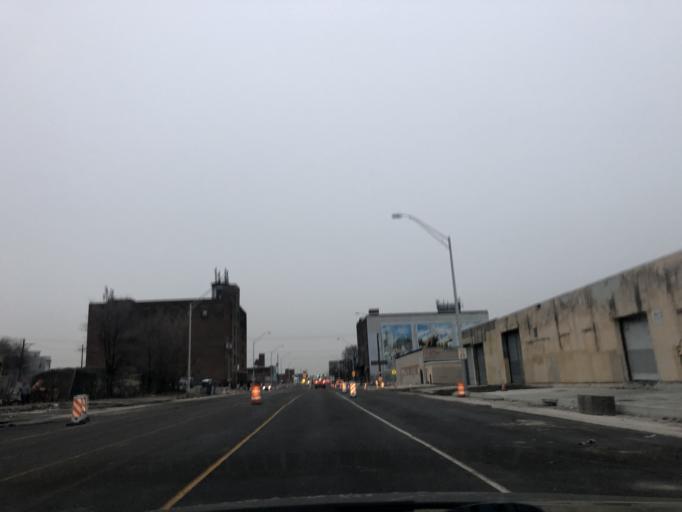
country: US
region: Pennsylvania
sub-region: Philadelphia County
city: Philadelphia
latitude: 39.9858
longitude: -75.1374
